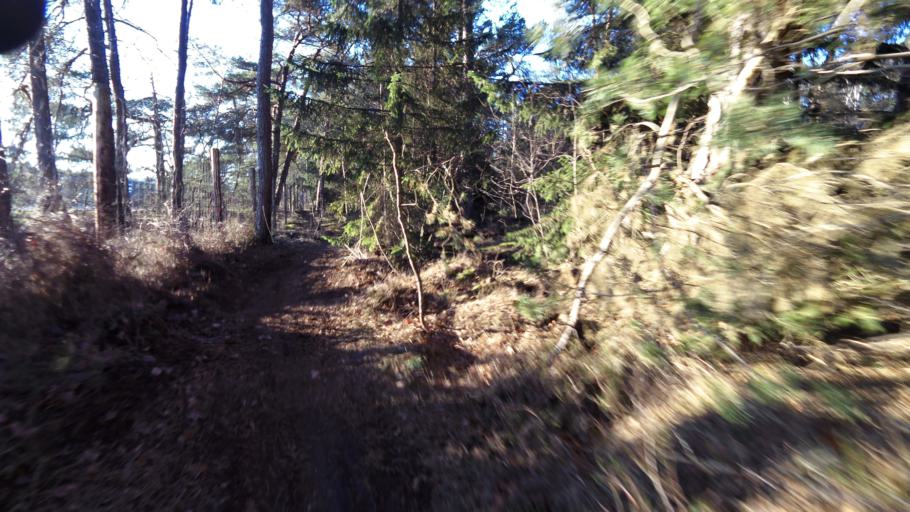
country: NL
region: Gelderland
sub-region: Gemeente Barneveld
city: Garderen
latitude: 52.1947
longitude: 5.7308
